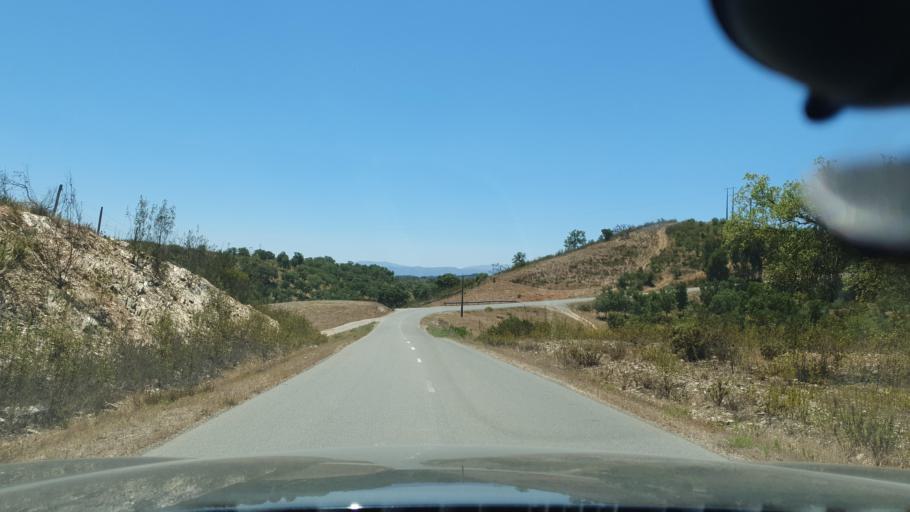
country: PT
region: Beja
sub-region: Odemira
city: Odemira
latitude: 37.5525
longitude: -8.4356
